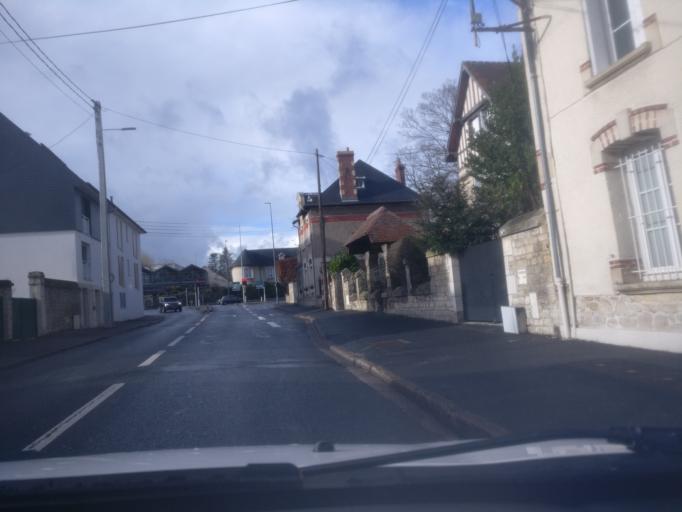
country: FR
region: Lower Normandy
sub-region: Departement du Calvados
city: Caen
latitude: 49.1914
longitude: -0.3743
